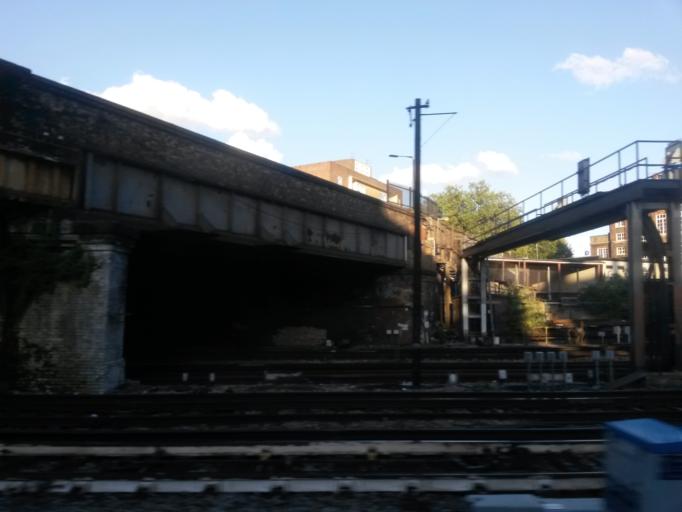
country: GB
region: England
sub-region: Greater London
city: Battersea
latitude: 51.4900
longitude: -0.1485
